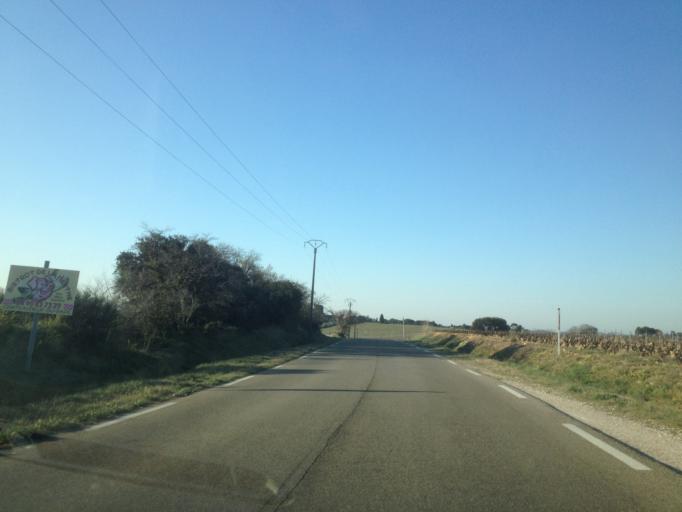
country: FR
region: Provence-Alpes-Cote d'Azur
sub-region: Departement du Vaucluse
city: Chateauneuf-du-Pape
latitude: 44.0658
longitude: 4.8288
